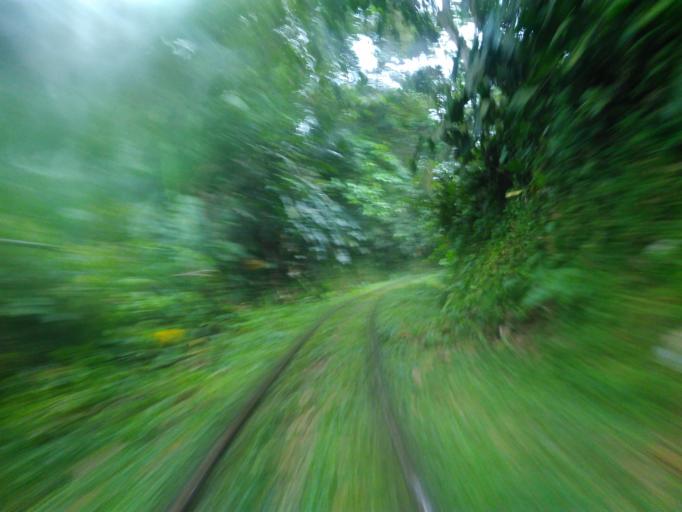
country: CO
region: Valle del Cauca
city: Buenaventura
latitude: 3.8462
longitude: -76.8668
